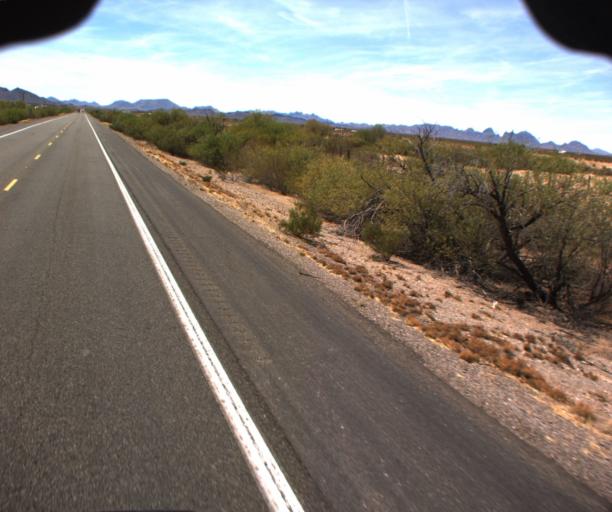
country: US
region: Arizona
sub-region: La Paz County
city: Salome
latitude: 33.7035
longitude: -113.8416
